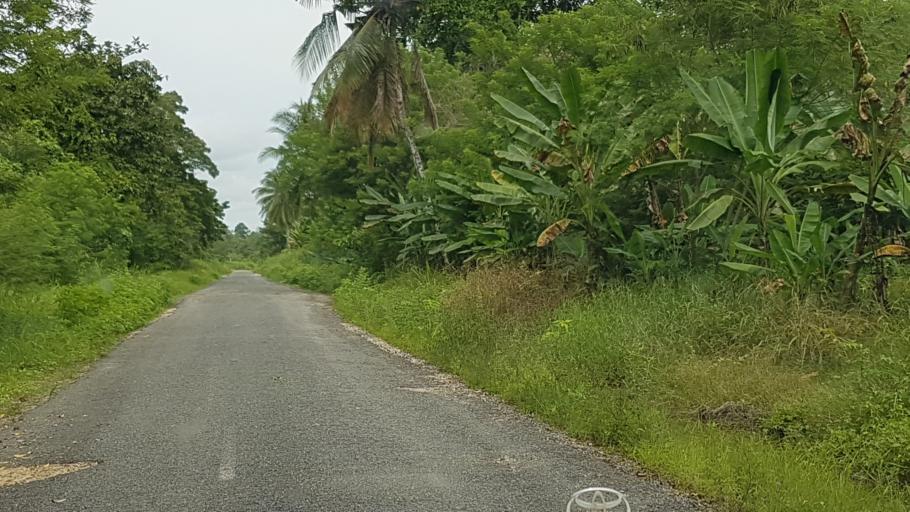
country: PG
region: Madang
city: Madang
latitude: -4.6856
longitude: 145.6006
